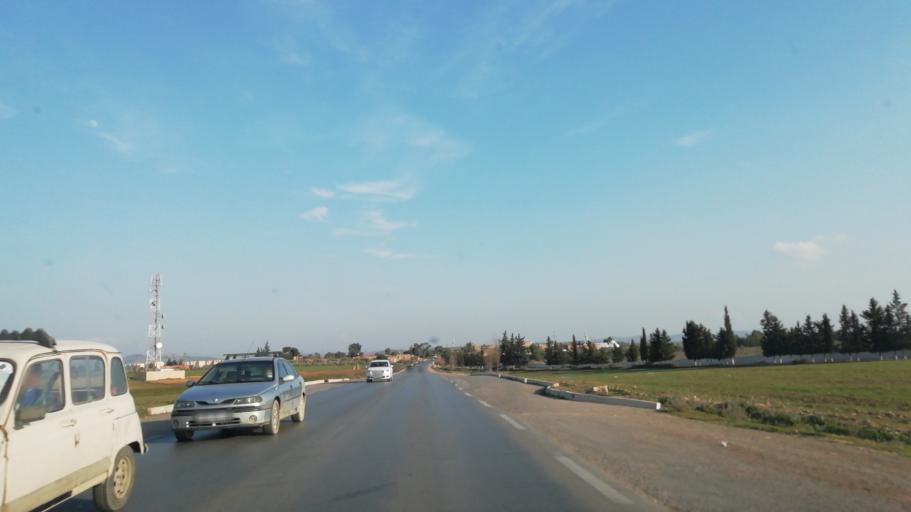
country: DZ
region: Relizane
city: Djidiouia
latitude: 35.8953
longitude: 0.7167
